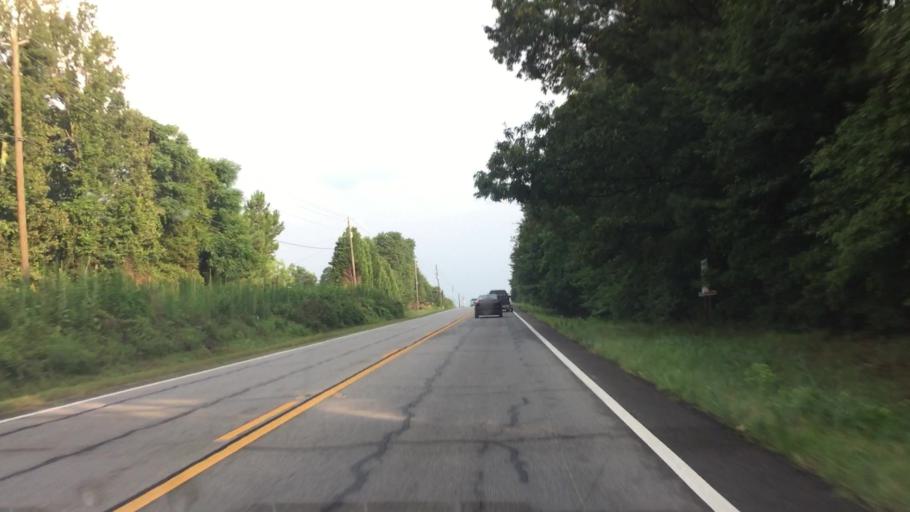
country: US
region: Georgia
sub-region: DeKalb County
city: Pine Mountain
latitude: 33.6158
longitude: -84.1685
